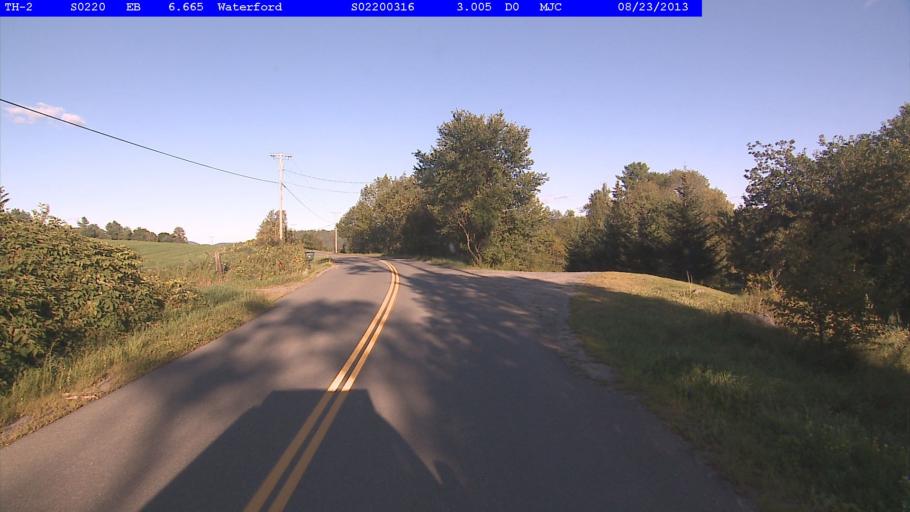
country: US
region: Vermont
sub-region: Caledonia County
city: Saint Johnsbury
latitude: 44.3395
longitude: -71.9436
